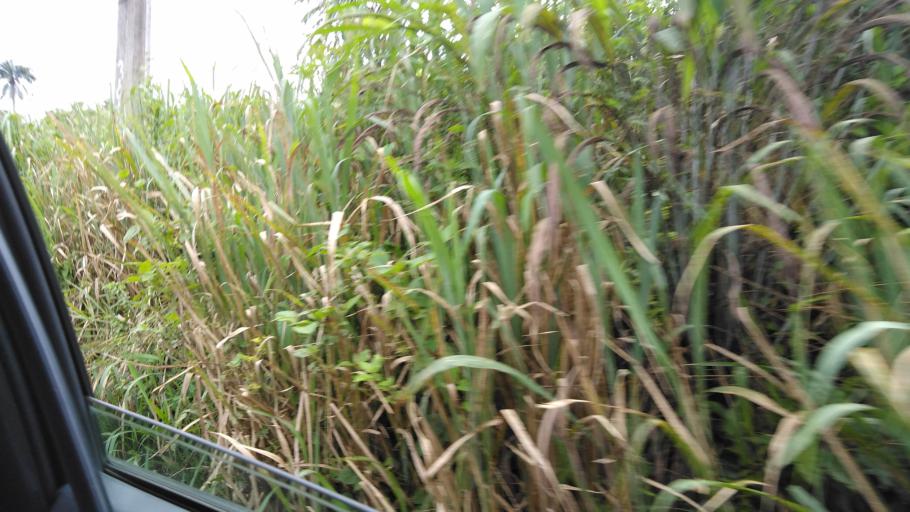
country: NG
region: Ogun
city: Abigi
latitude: 6.5713
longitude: 4.5599
